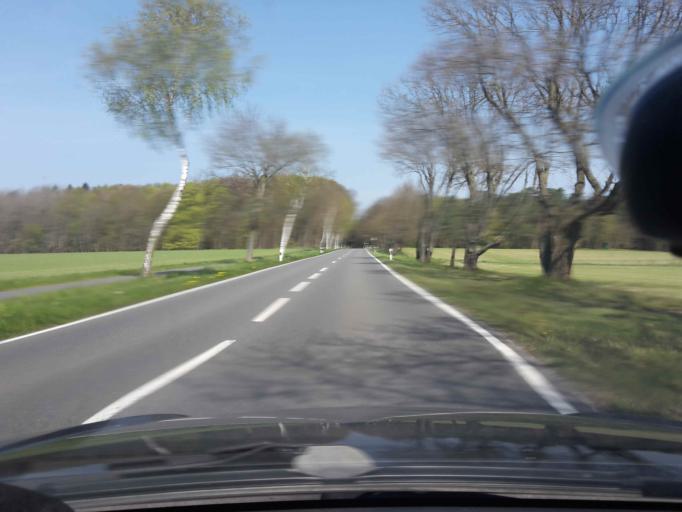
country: DE
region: Lower Saxony
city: Schneverdingen
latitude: 53.0886
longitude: 9.8479
